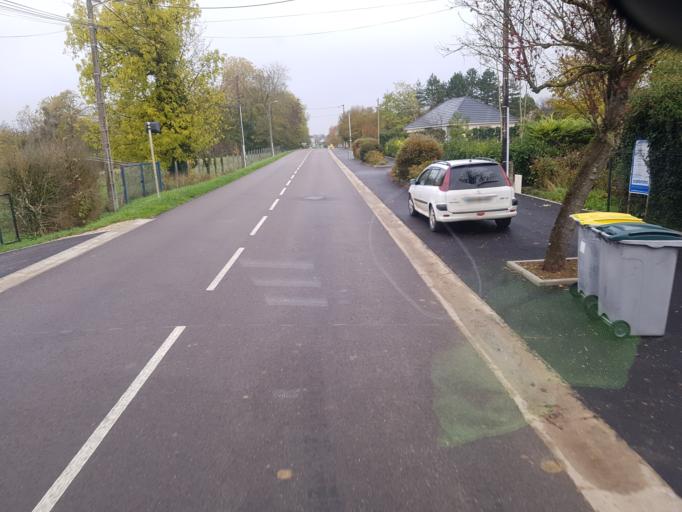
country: FR
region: Bourgogne
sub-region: Departement de la Cote-d'Or
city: Saint-Julien
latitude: 47.3988
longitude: 5.1967
